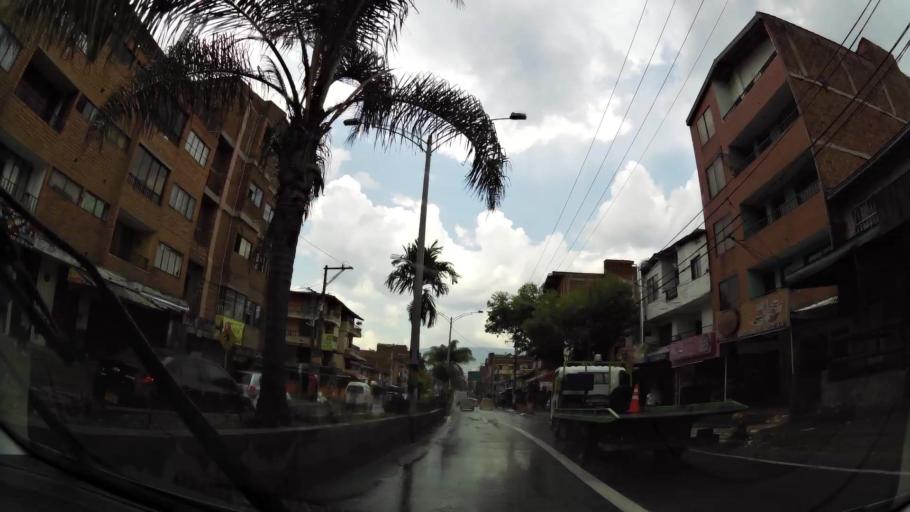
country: CO
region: Antioquia
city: Itagui
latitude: 6.1843
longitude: -75.5970
